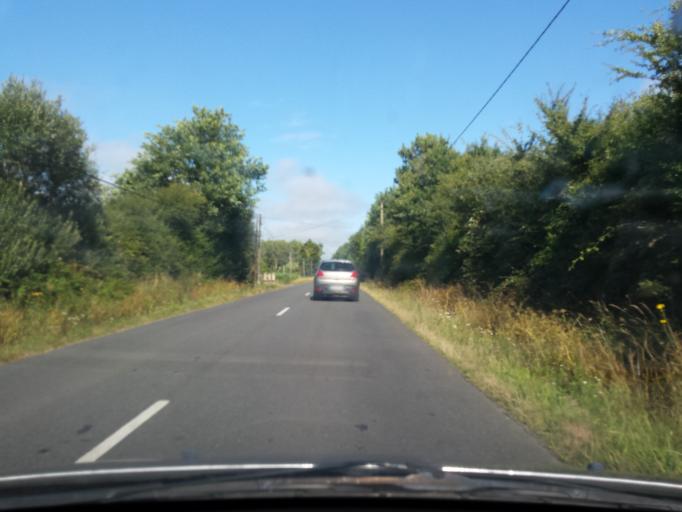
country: FR
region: Pays de la Loire
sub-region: Departement de la Vendee
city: Vaire
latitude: 46.6473
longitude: -1.7946
